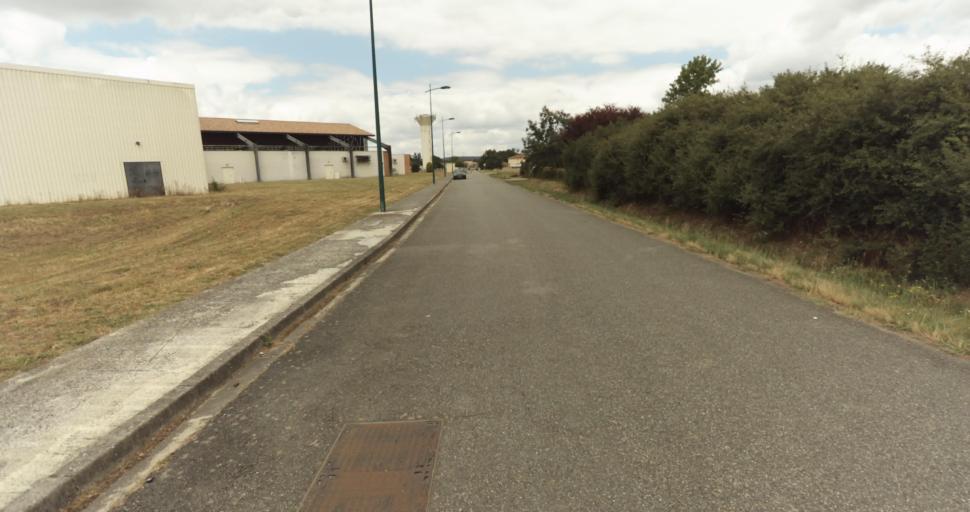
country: FR
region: Midi-Pyrenees
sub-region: Departement de la Haute-Garonne
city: Fontenilles
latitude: 43.5474
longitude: 1.1943
